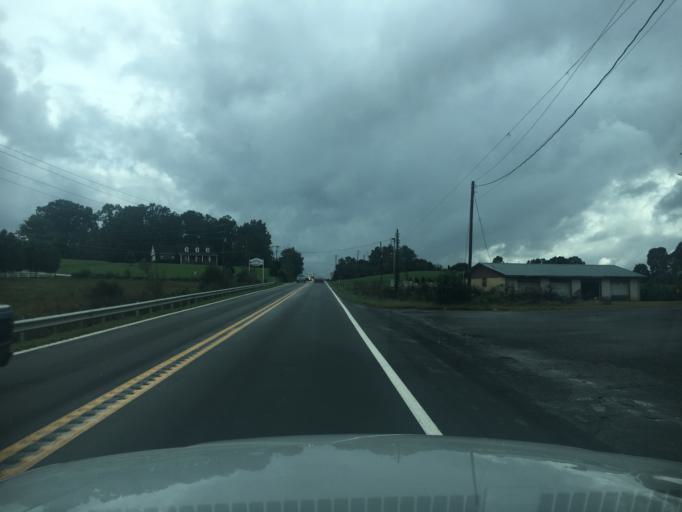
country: US
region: North Carolina
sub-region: Burke County
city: Salem
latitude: 35.6831
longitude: -81.7293
